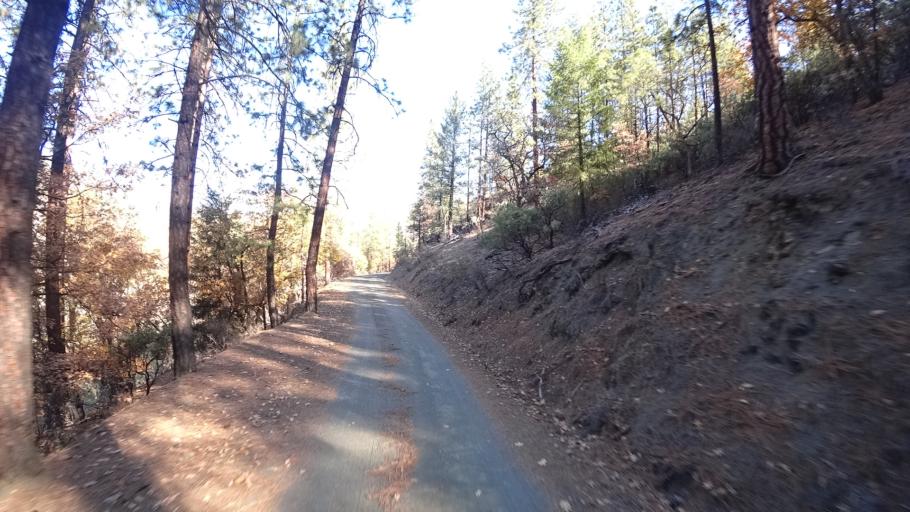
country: US
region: California
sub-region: Siskiyou County
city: Yreka
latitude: 41.8567
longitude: -122.8269
